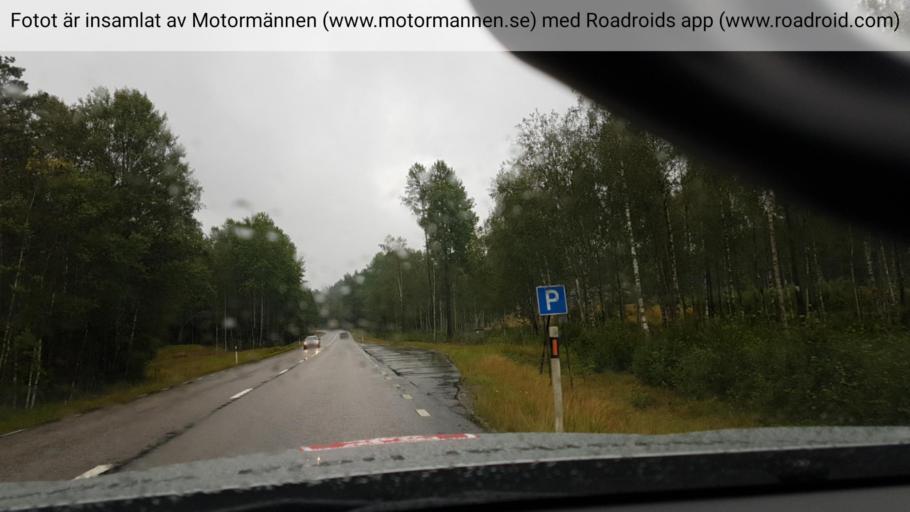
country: SE
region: Vaestra Goetaland
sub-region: Dals-Ed Kommun
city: Ed
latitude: 58.8769
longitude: 11.8309
